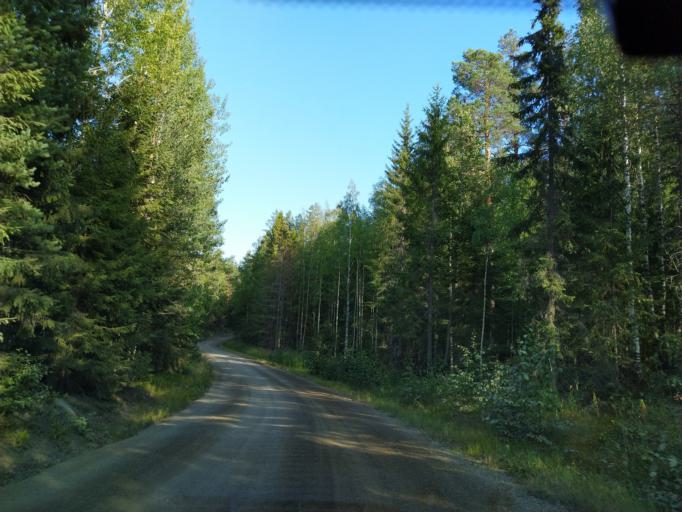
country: FI
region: Central Finland
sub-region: Jaemsae
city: Kuhmoinen
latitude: 61.6822
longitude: 24.9758
